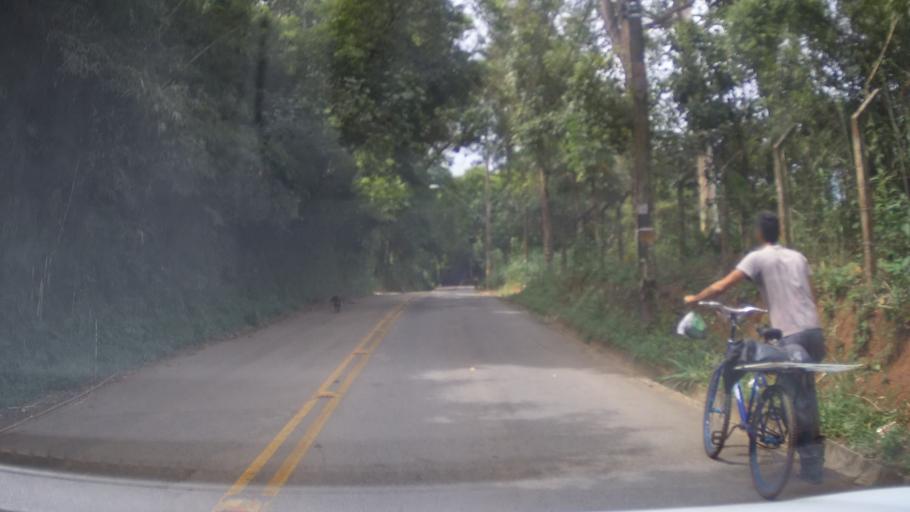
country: BR
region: Sao Paulo
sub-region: Aruja
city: Aruja
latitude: -23.3847
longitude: -46.3969
